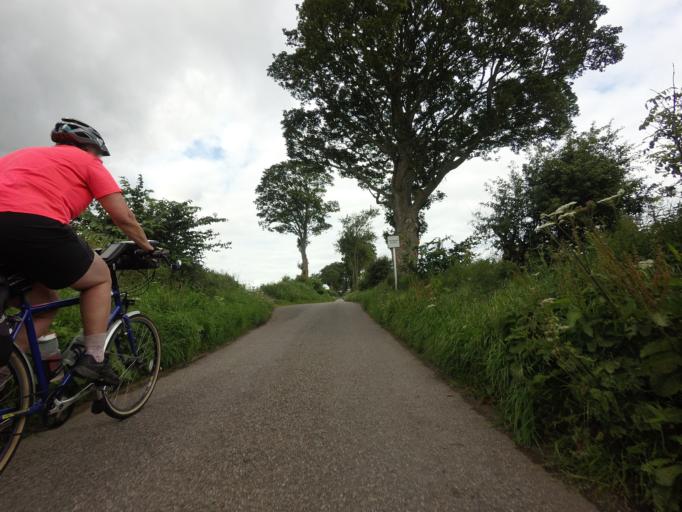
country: GB
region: Scotland
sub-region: Moray
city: Forres
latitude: 57.6133
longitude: -3.6482
